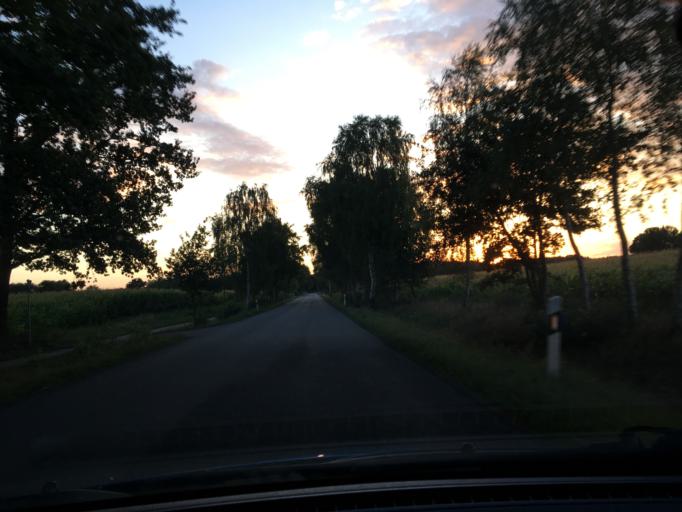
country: DE
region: Lower Saxony
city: Fassberg
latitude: 52.8958
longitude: 10.1426
